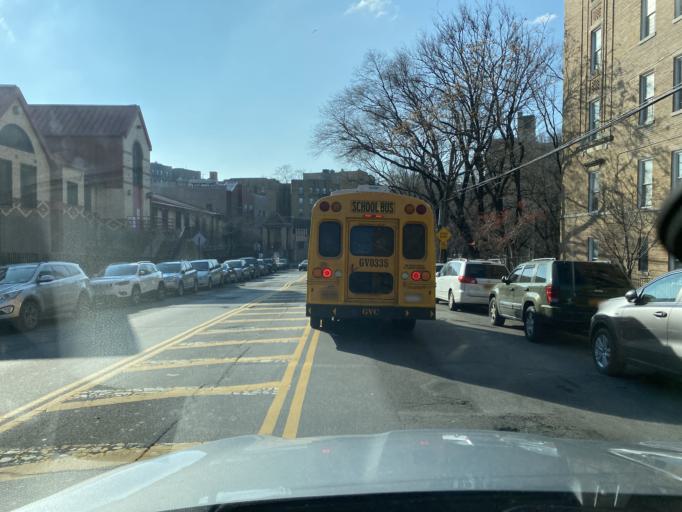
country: US
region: New York
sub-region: New York County
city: Inwood
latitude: 40.8560
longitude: -73.9163
